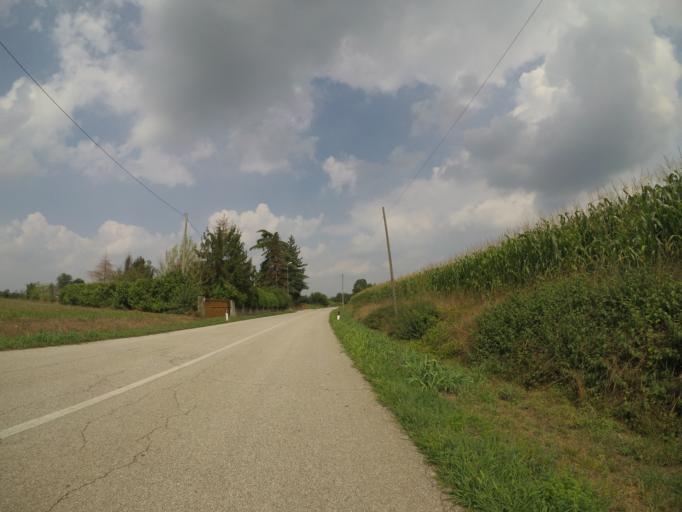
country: IT
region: Friuli Venezia Giulia
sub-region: Provincia di Udine
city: Sedegliano
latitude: 46.0052
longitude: 13.0025
